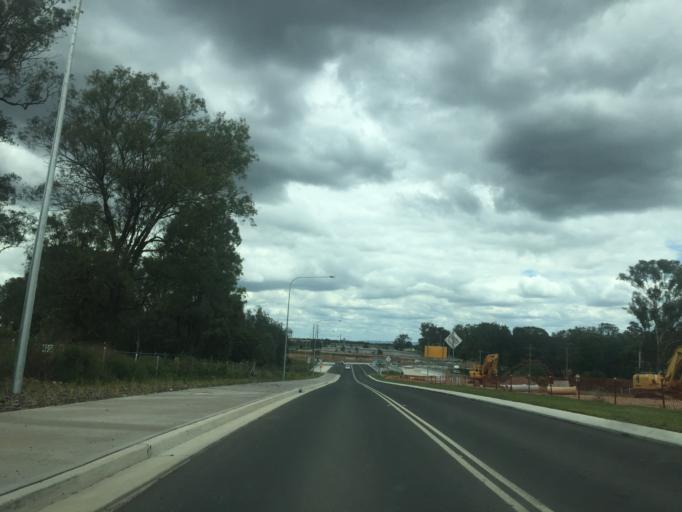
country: AU
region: New South Wales
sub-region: Blacktown
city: Riverstone
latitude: -33.7004
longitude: 150.8765
